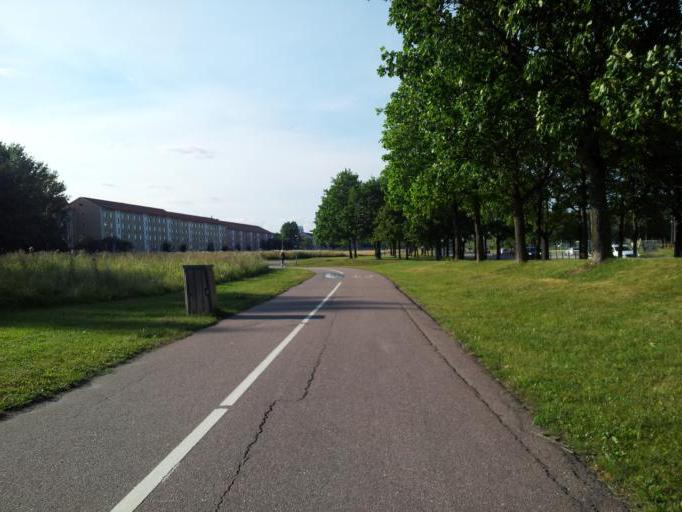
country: SE
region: Uppsala
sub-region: Uppsala Kommun
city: Uppsala
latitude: 59.8643
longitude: 17.6820
